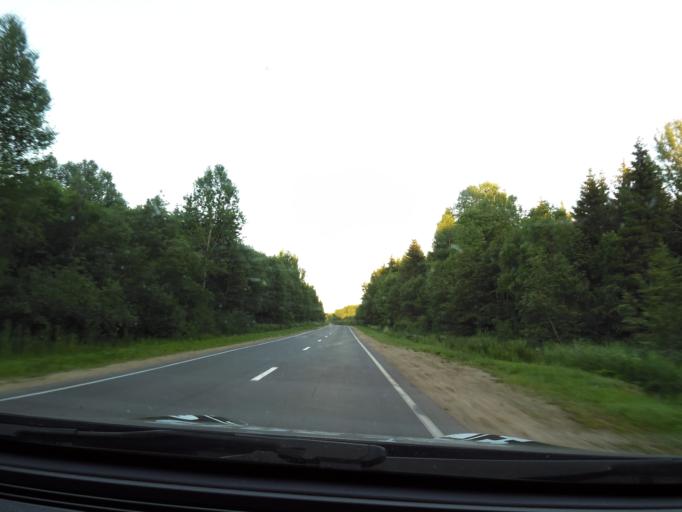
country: RU
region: Jaroslavl
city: Prechistoye
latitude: 58.3986
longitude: 40.3983
